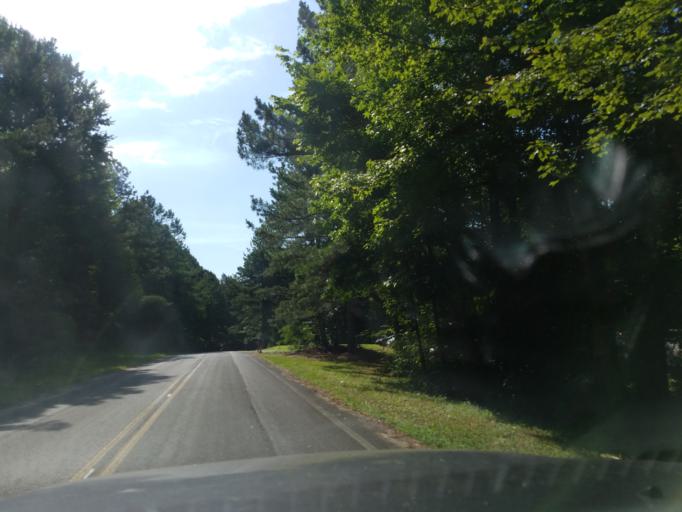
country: US
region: North Carolina
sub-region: Vance County
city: Henderson
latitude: 36.3429
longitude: -78.4220
